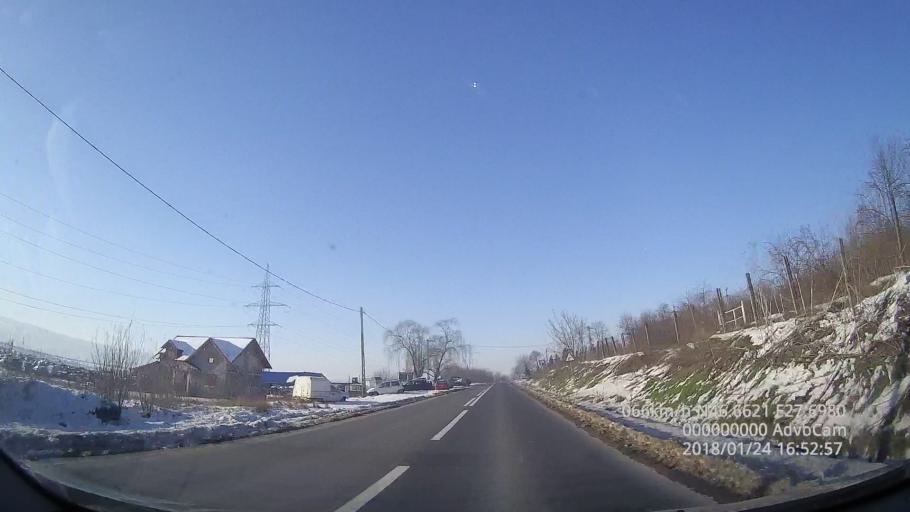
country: RO
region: Vaslui
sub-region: Municipiul Vaslui
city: Brodoc
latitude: 46.6623
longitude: 27.6976
